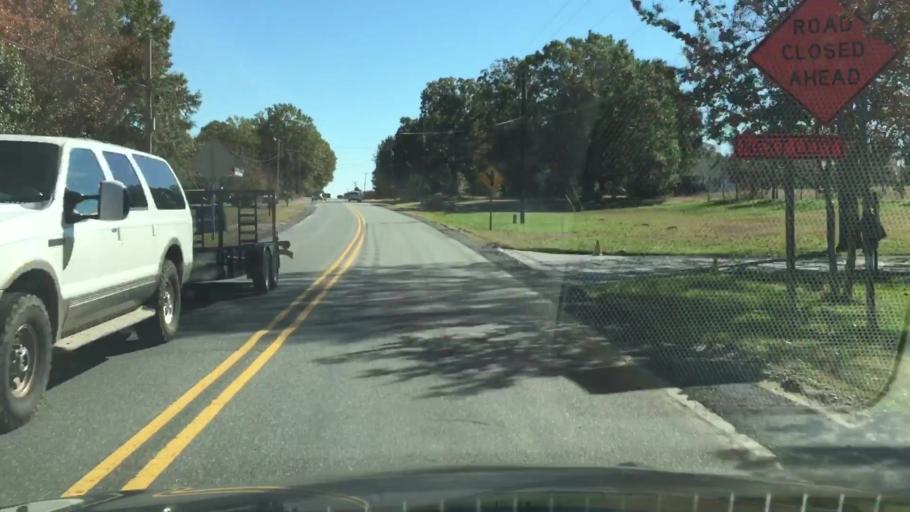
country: US
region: North Carolina
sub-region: Rockingham County
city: Reidsville
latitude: 36.2976
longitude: -79.6627
